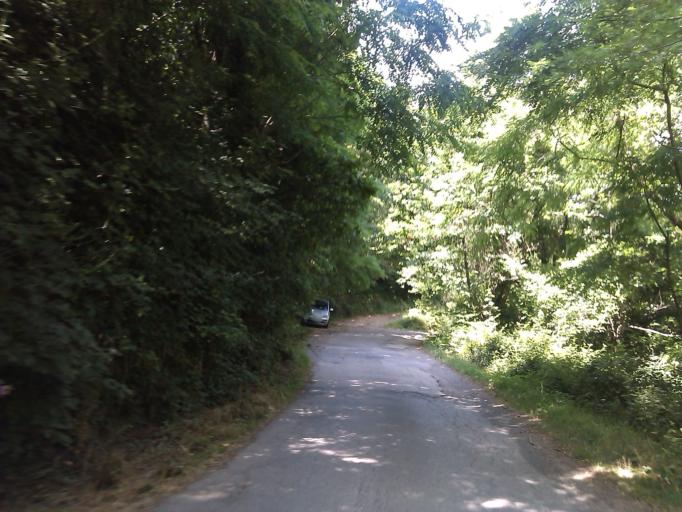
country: IT
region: Tuscany
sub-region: Provincia di Pistoia
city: Montale
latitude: 43.9687
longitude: 11.0408
